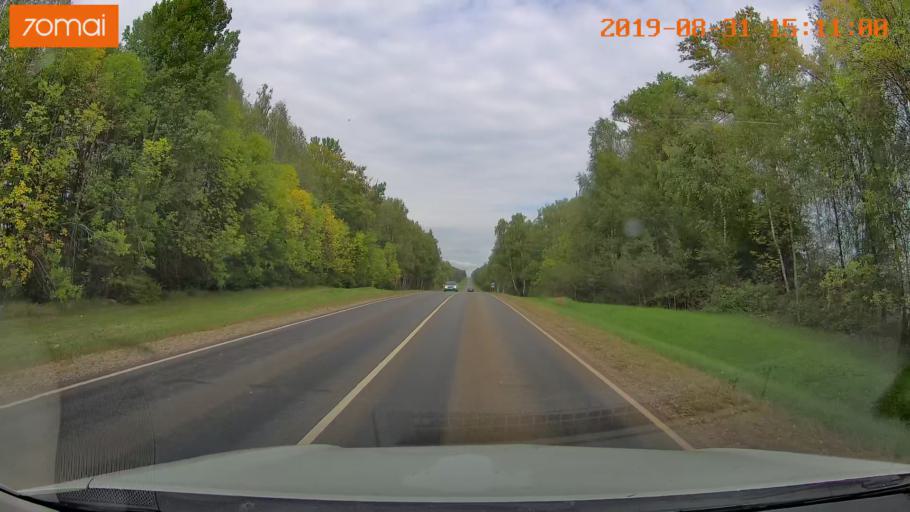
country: RU
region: Kaluga
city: Spas-Demensk
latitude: 54.4188
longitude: 34.2332
